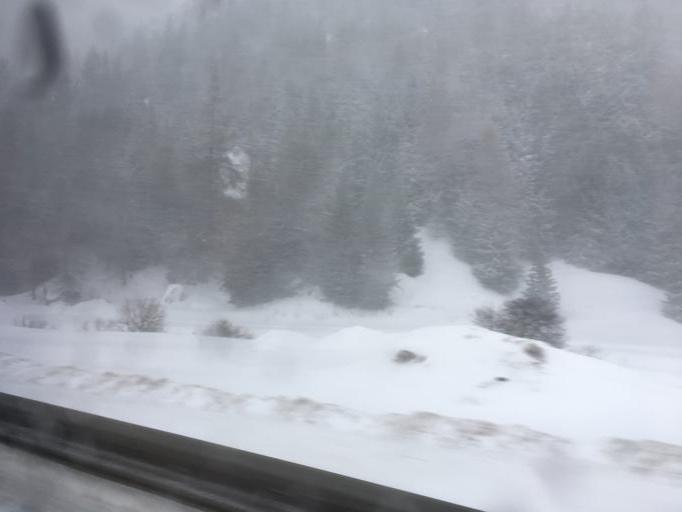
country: CH
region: Grisons
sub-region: Maloja District
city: Silvaplana
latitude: 46.4729
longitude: 9.6496
